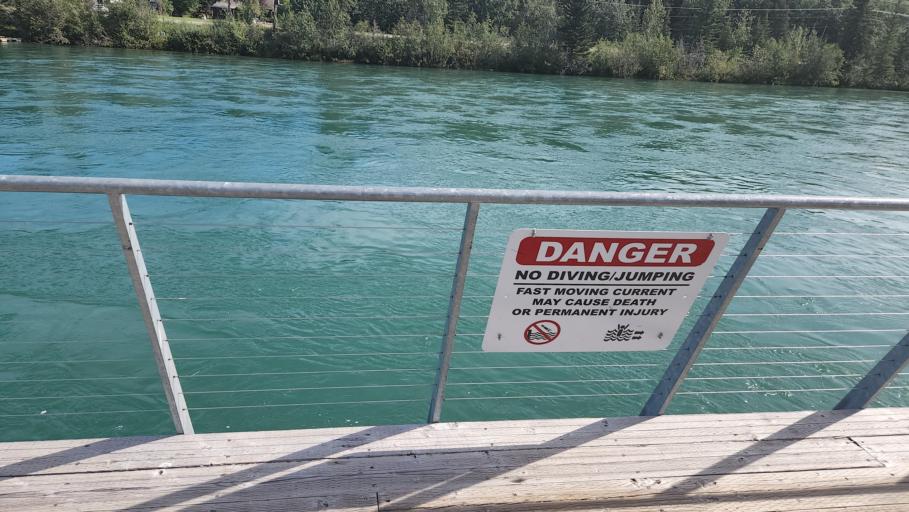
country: CA
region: Yukon
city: Whitehorse
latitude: 60.7205
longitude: -135.0495
